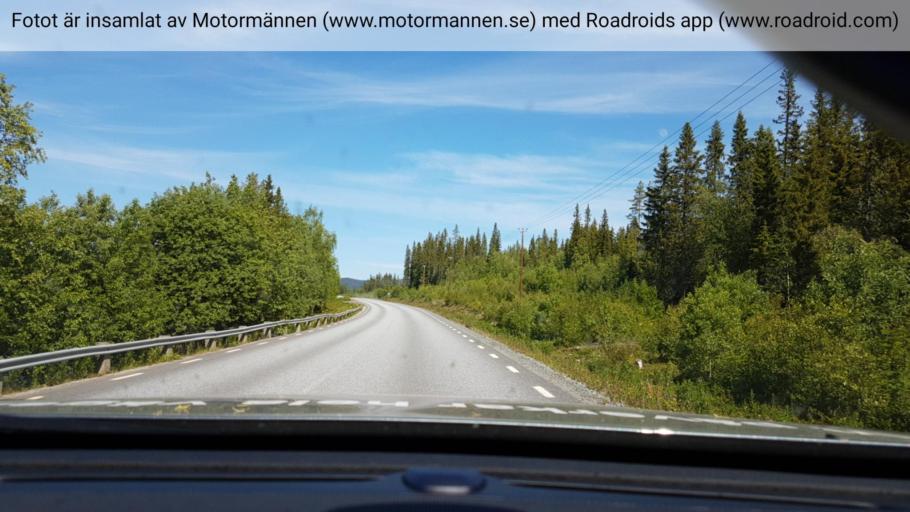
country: SE
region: Vaesterbotten
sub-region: Vilhelmina Kommun
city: Sjoberg
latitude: 64.6811
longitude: 15.5690
